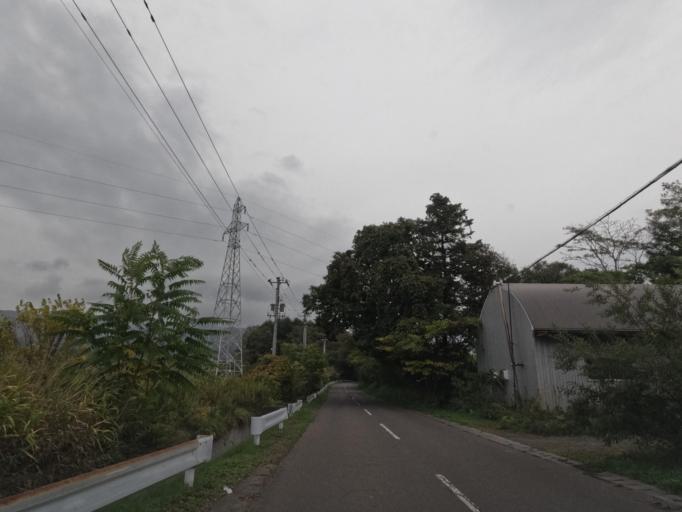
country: JP
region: Hokkaido
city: Date
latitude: 42.4749
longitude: 140.8882
